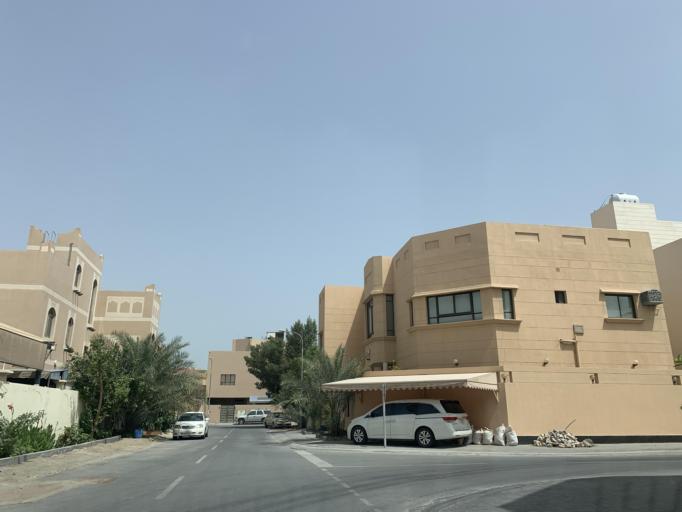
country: BH
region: Northern
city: Sitrah
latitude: 26.1365
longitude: 50.6030
